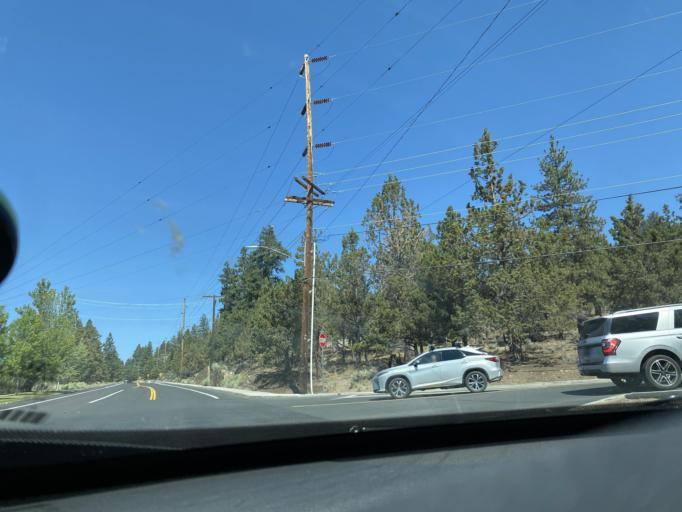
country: US
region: Oregon
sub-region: Deschutes County
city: Bend
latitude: 44.0641
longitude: -121.3390
